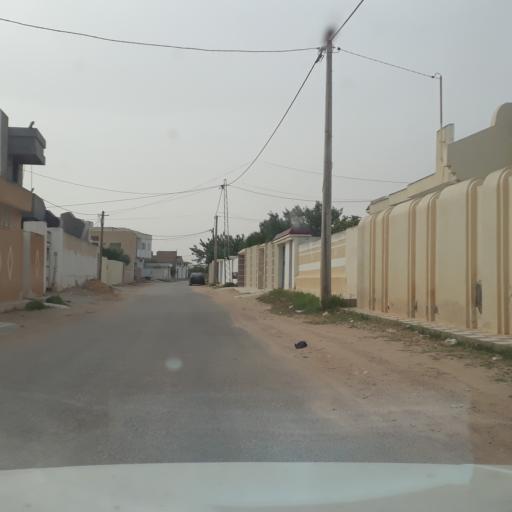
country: TN
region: Safaqis
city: Al Qarmadah
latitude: 34.8202
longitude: 10.7734
